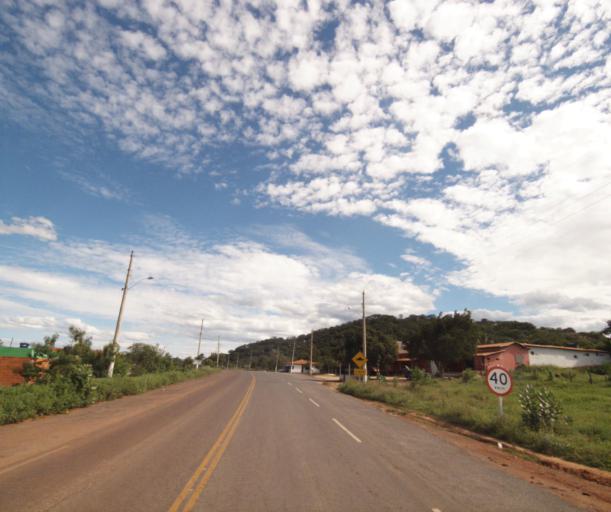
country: BR
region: Minas Gerais
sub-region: Espinosa
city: Espinosa
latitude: -14.8501
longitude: -42.7584
